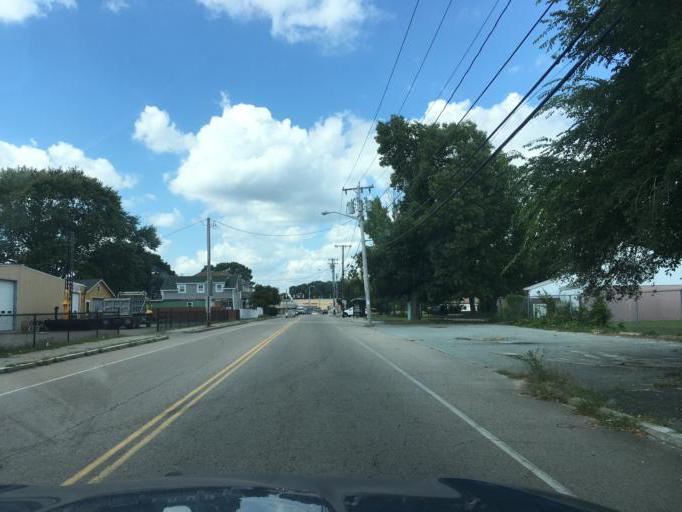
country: US
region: Rhode Island
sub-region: Kent County
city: Warwick
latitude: 41.6993
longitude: -71.3989
